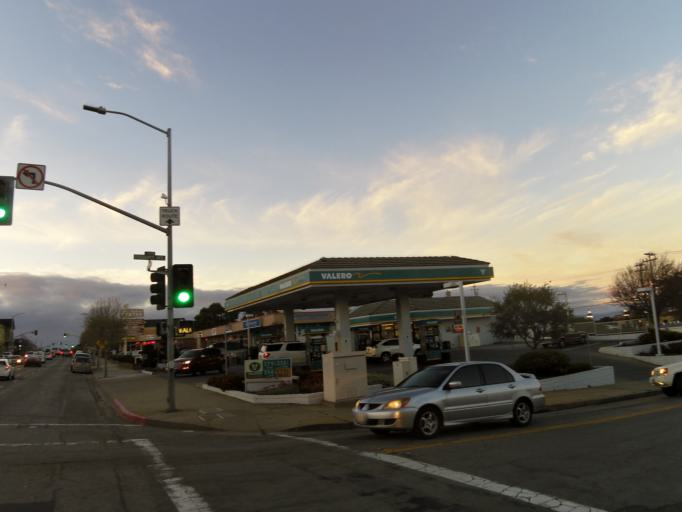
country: US
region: California
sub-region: Monterey County
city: Pacific Grove
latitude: 36.6147
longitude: -121.9026
